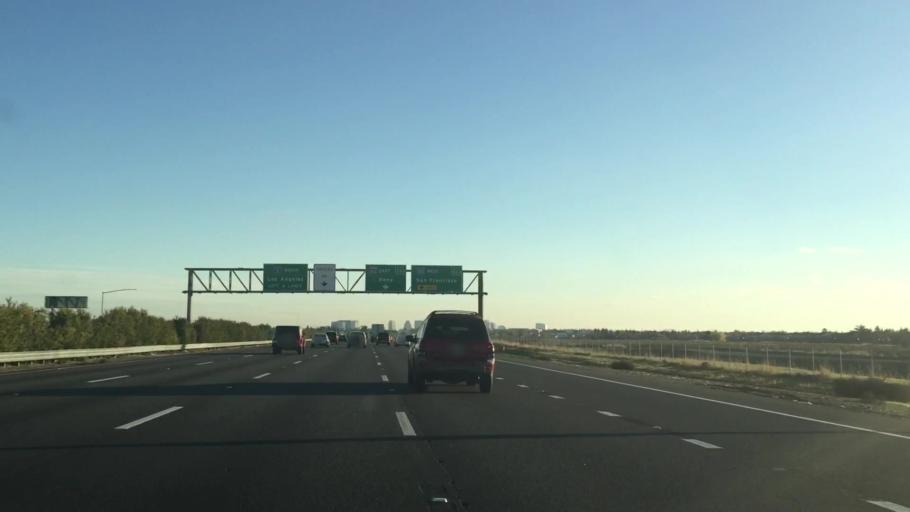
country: US
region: California
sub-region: Yolo County
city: West Sacramento
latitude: 38.6395
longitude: -121.5245
